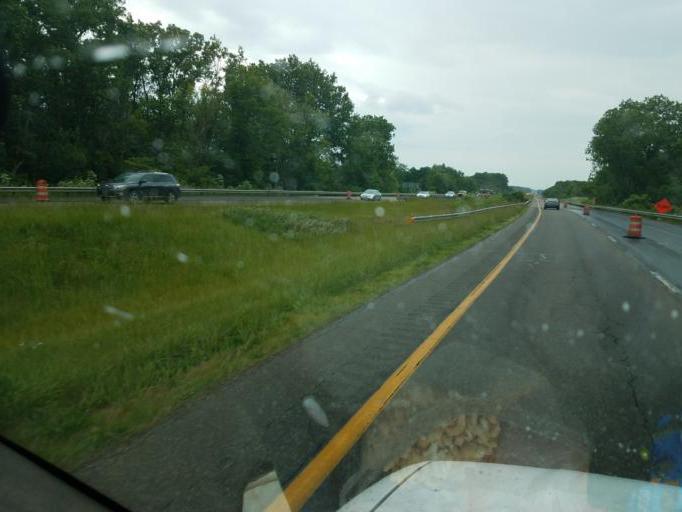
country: US
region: Ohio
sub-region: Ashland County
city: Loudonville
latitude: 40.7853
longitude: -82.1639
